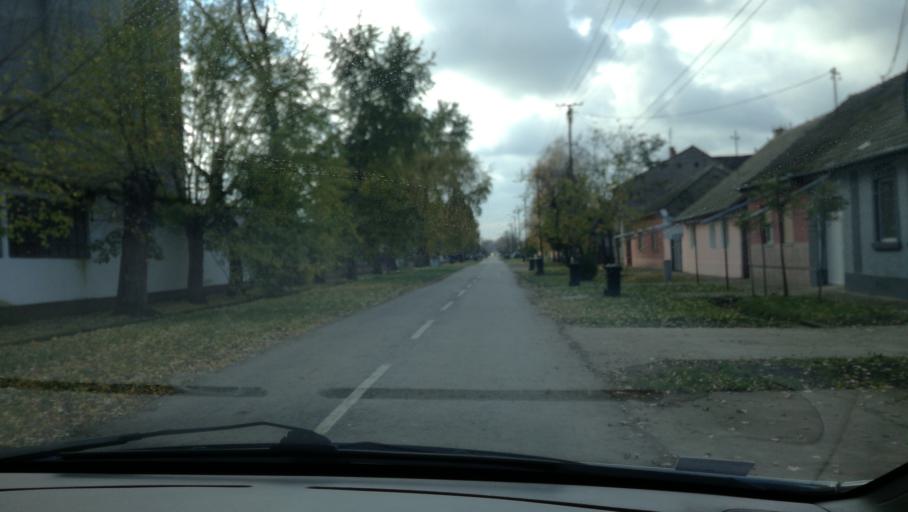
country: RS
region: Autonomna Pokrajina Vojvodina
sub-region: Severnobanatski Okrug
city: Kikinda
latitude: 45.8398
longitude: 20.4843
